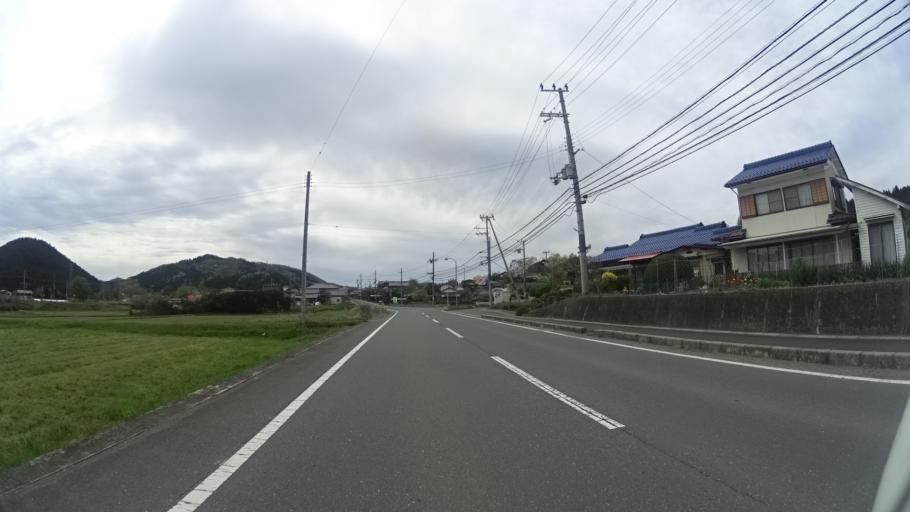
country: JP
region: Kyoto
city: Kameoka
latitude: 35.1955
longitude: 135.4730
